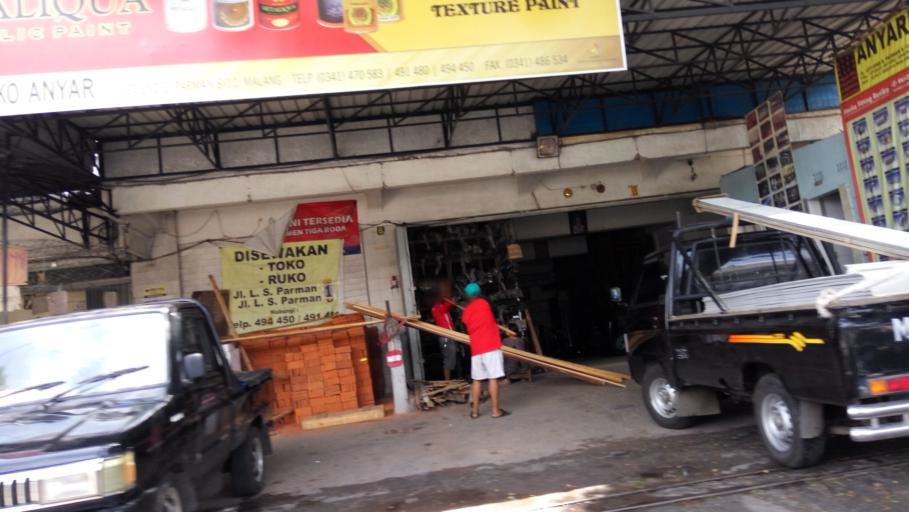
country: ID
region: East Java
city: Malang
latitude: -7.9548
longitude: 112.6386
